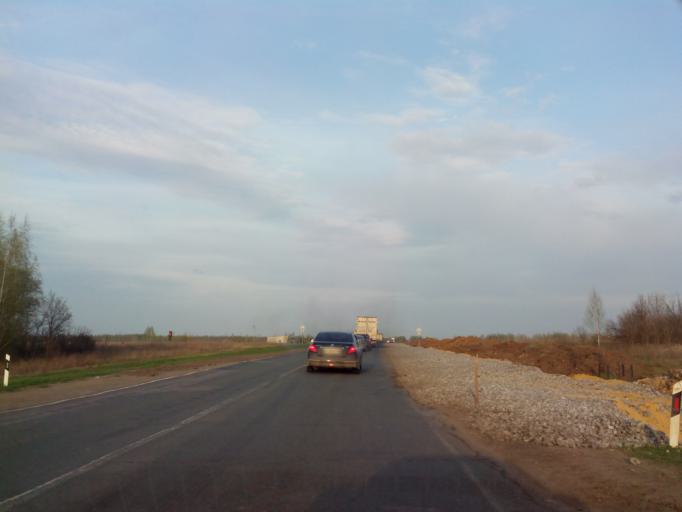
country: RU
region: Rjazan
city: Zarechnyy
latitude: 53.7522
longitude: 39.8329
